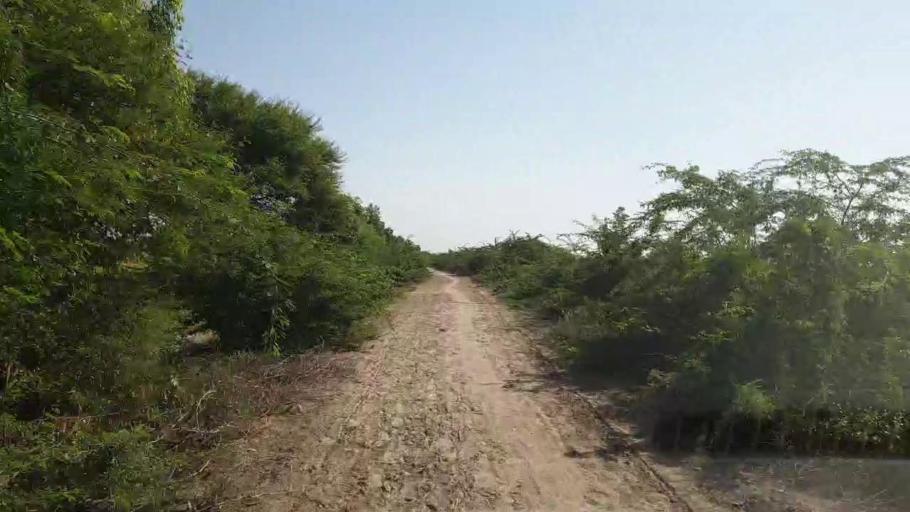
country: PK
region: Sindh
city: Kadhan
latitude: 24.5861
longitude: 69.0104
